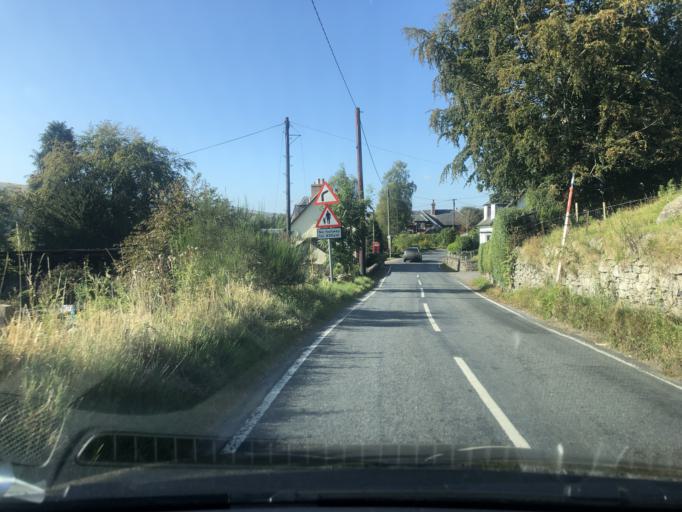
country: GB
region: Scotland
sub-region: Perth and Kinross
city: Blairgowrie
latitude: 56.6778
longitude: -3.4674
